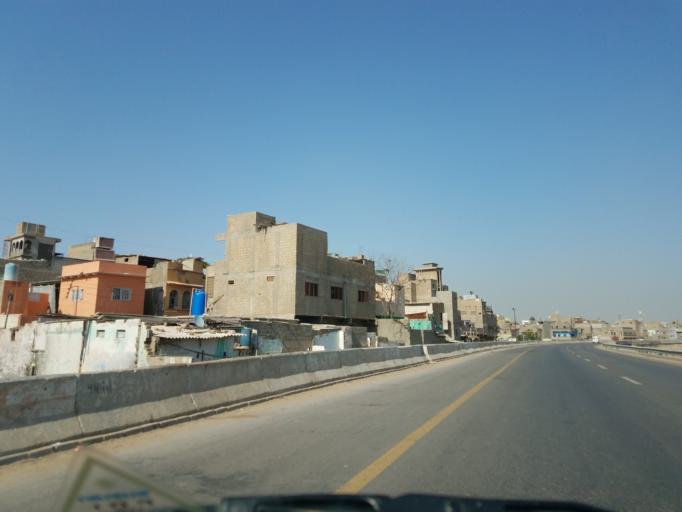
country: PK
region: Sindh
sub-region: Karachi District
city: Karachi
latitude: 24.8880
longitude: 67.0246
